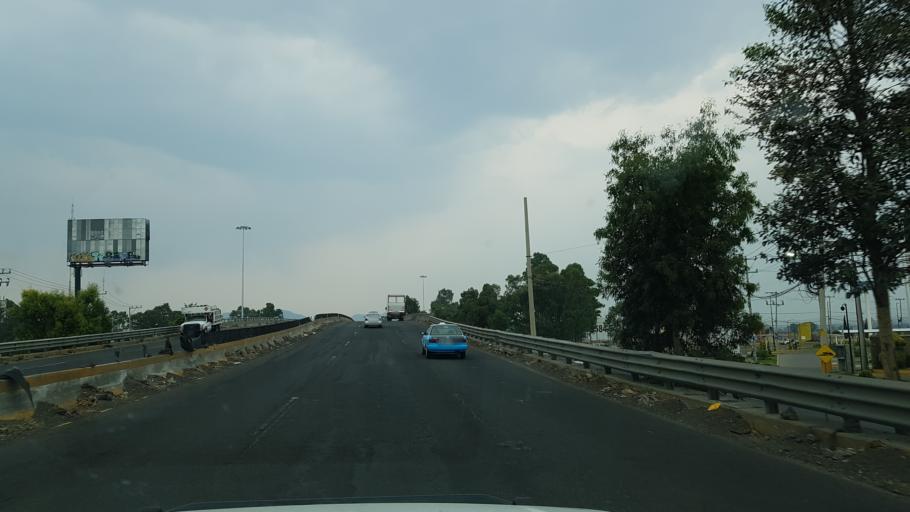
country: MX
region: Mexico
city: Chalco de Diaz Covarrubias
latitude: 19.2600
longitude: -98.8798
